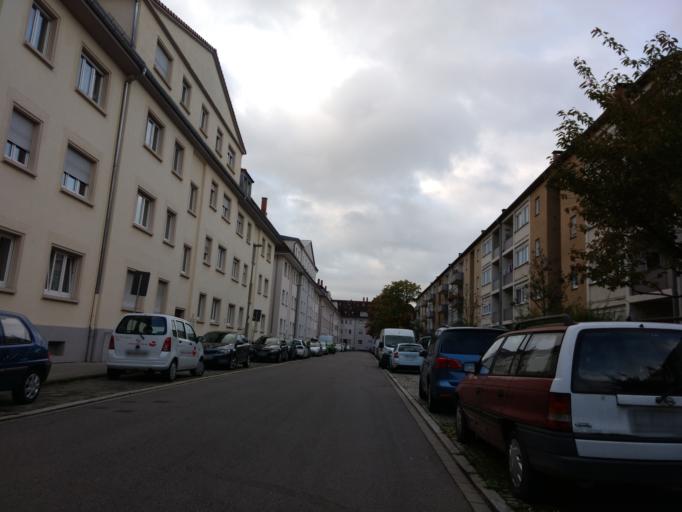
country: DE
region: Baden-Wuerttemberg
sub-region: Karlsruhe Region
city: Karlsruhe
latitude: 49.0128
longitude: 8.4210
